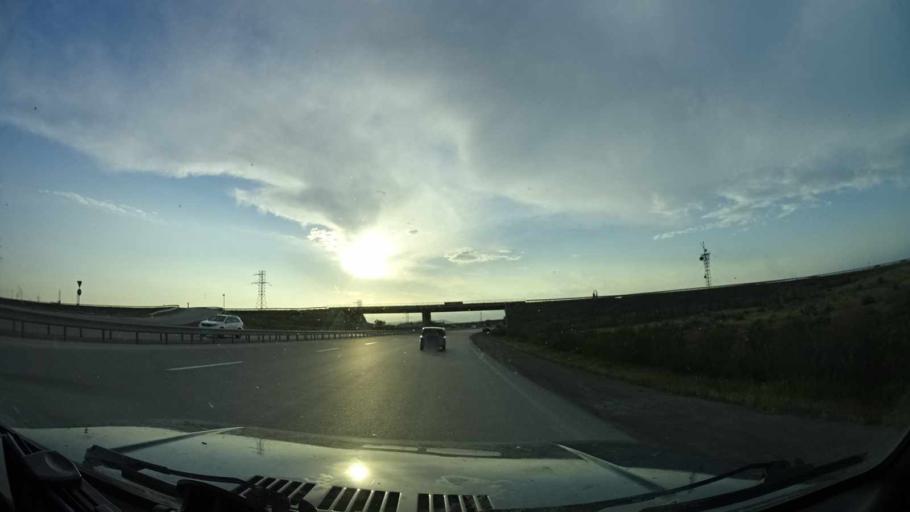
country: AZ
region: Abseron
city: Ceyranbatan
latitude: 40.5535
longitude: 49.6215
